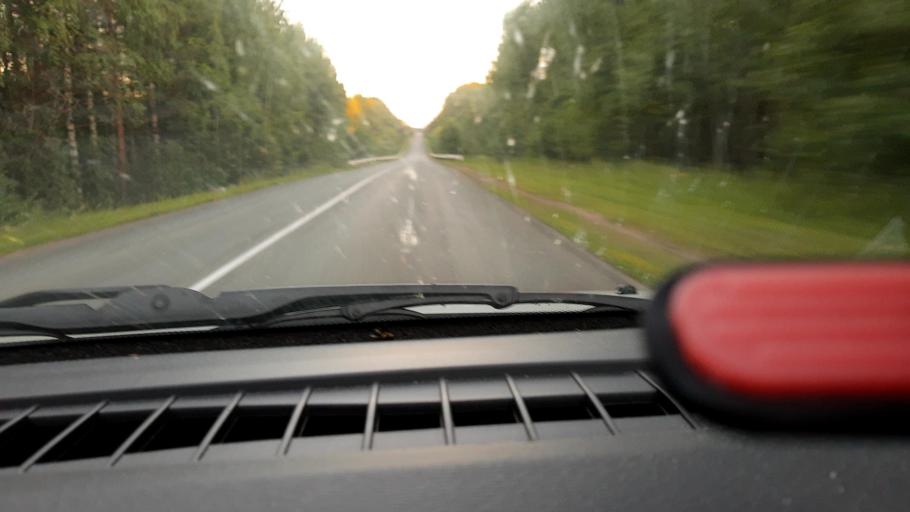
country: RU
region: Nizjnij Novgorod
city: Tonkino
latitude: 57.2974
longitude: 46.4624
